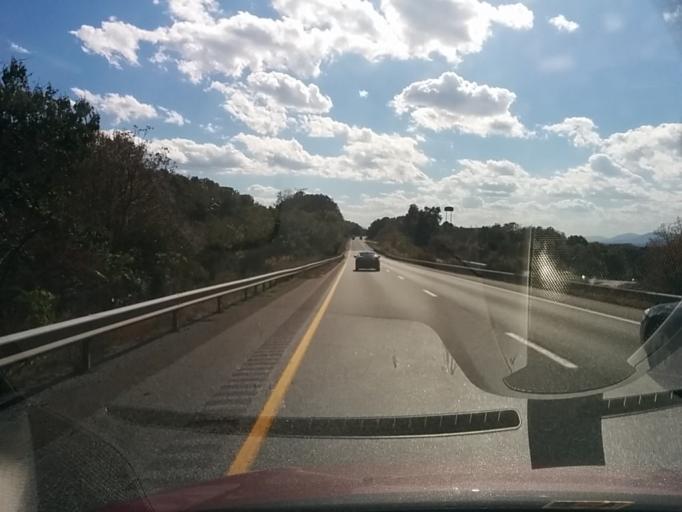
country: US
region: Virginia
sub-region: Rockbridge County
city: East Lexington
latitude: 37.8430
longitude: -79.3665
